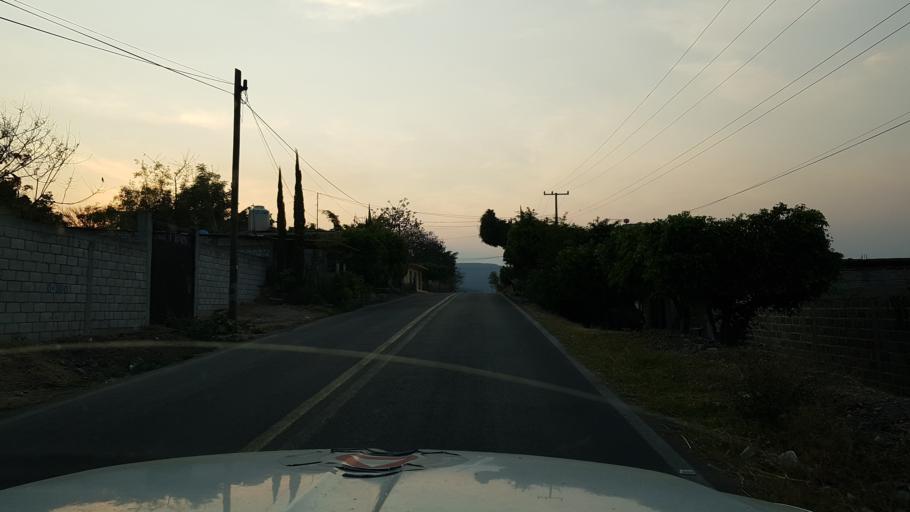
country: MX
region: Morelos
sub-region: Ayala
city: Abelardo L. Rodriguez
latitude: 18.7262
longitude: -98.9995
